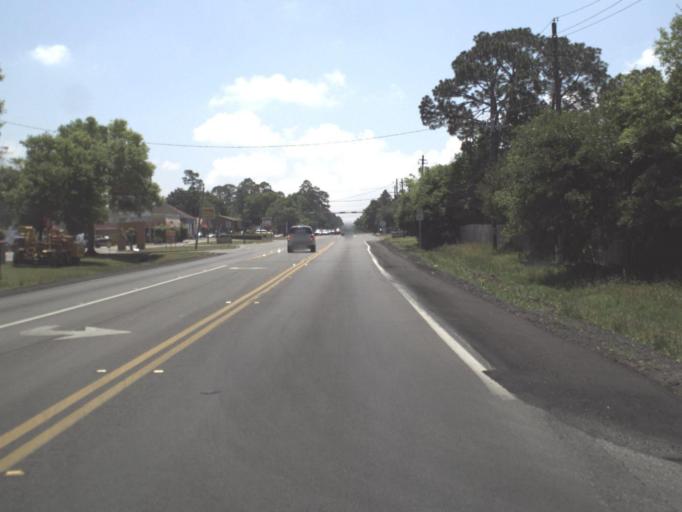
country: US
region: Florida
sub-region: Escambia County
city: Myrtle Grove
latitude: 30.4235
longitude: -87.3173
